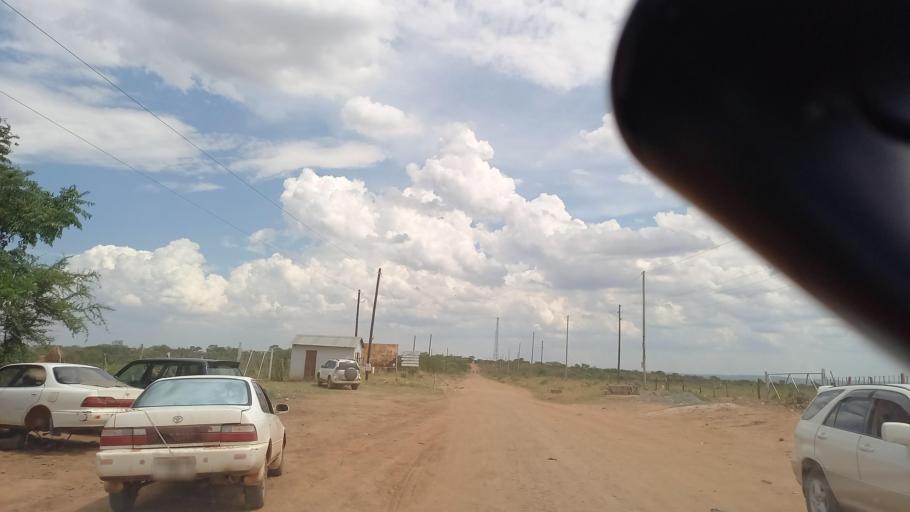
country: ZM
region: Southern
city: Nakambala
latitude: -16.0282
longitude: 27.9677
